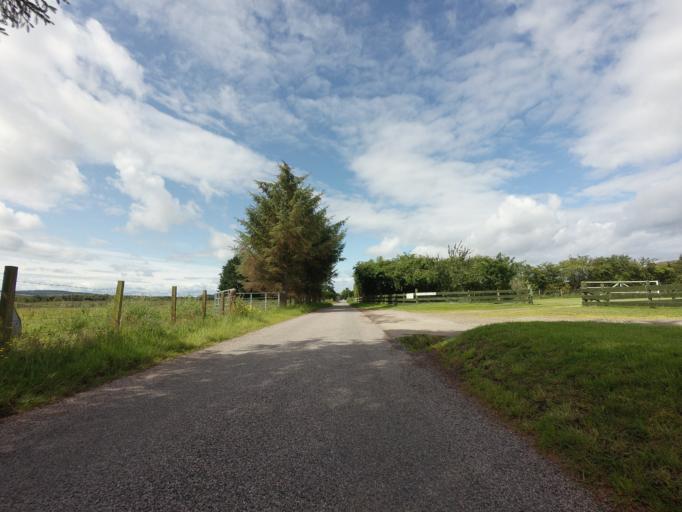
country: GB
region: Scotland
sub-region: Moray
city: Burghead
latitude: 57.6537
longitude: -3.4815
